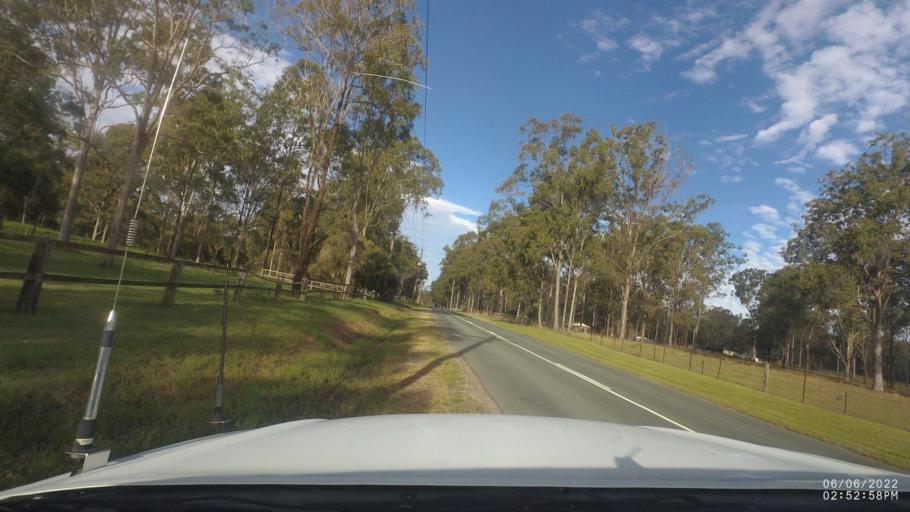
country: AU
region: Queensland
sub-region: Logan
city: Cedar Vale
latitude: -27.8527
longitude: 153.0388
